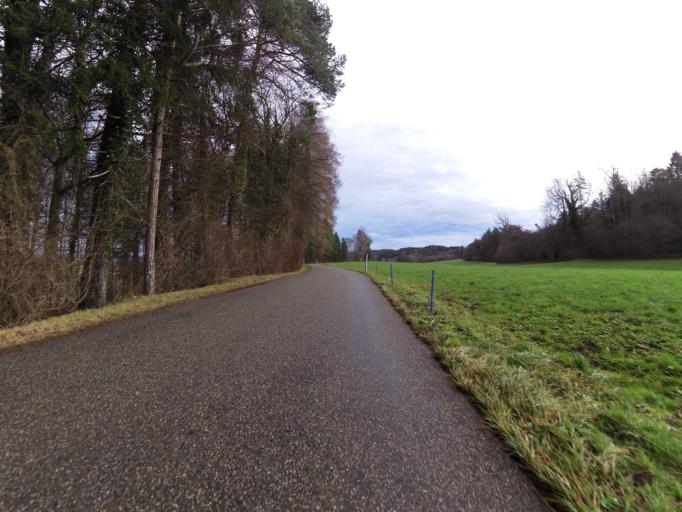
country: CH
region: Thurgau
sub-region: Frauenfeld District
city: Matzingen
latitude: 47.5528
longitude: 8.9310
